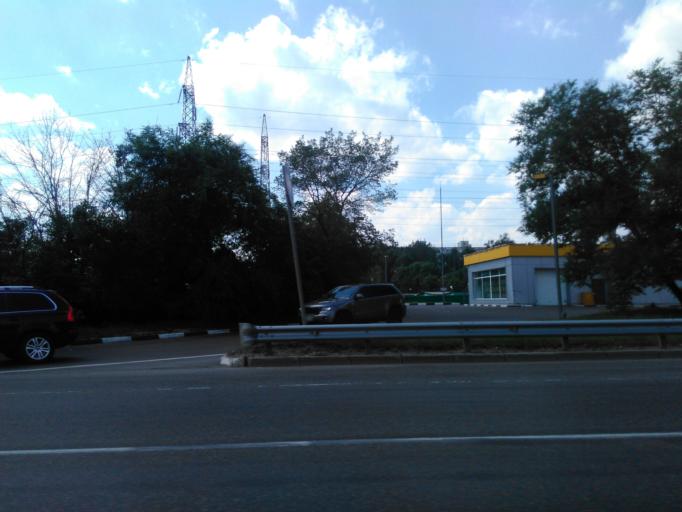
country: RU
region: Moskovskaya
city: Kuskovo
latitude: 55.7383
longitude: 37.8411
